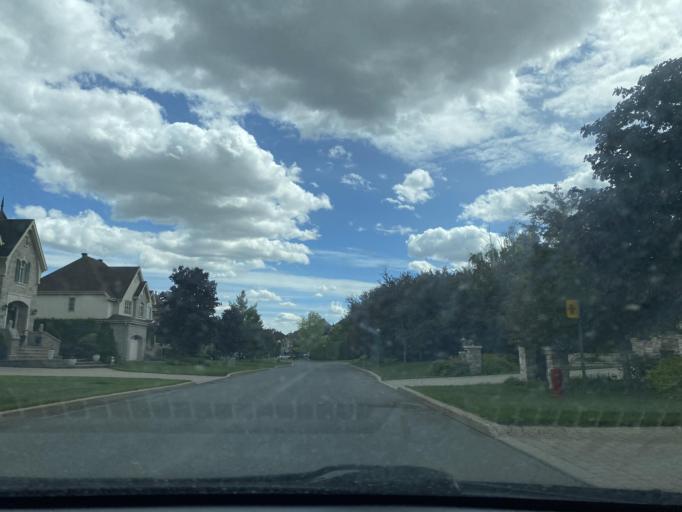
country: CA
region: Quebec
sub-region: Monteregie
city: Carignan
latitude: 45.4702
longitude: -73.2957
